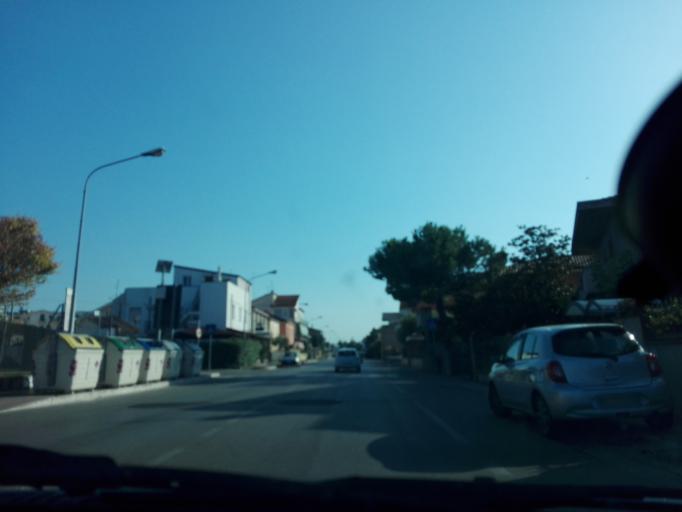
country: IT
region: Abruzzo
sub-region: Provincia di Pescara
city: Montesilvano Marina
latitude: 42.4963
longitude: 14.1279
